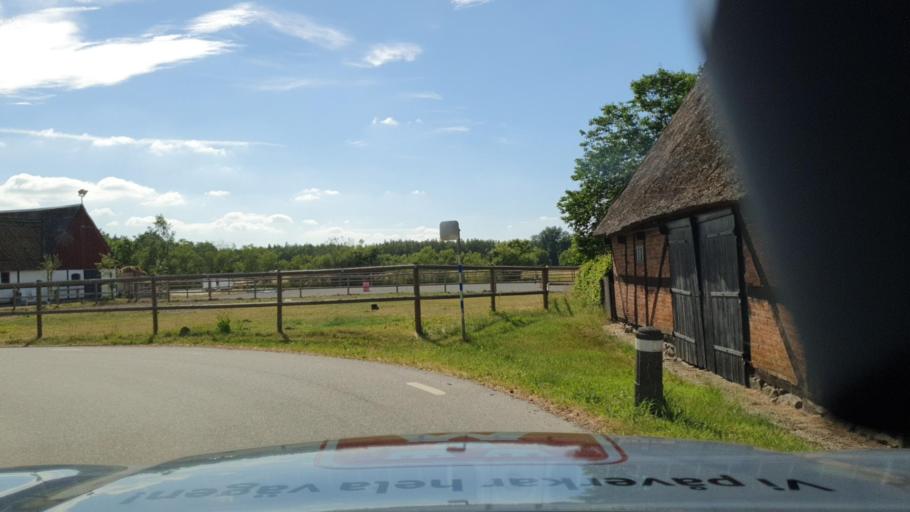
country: SE
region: Skane
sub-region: Sjobo Kommun
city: Blentarp
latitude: 55.6084
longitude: 13.6185
